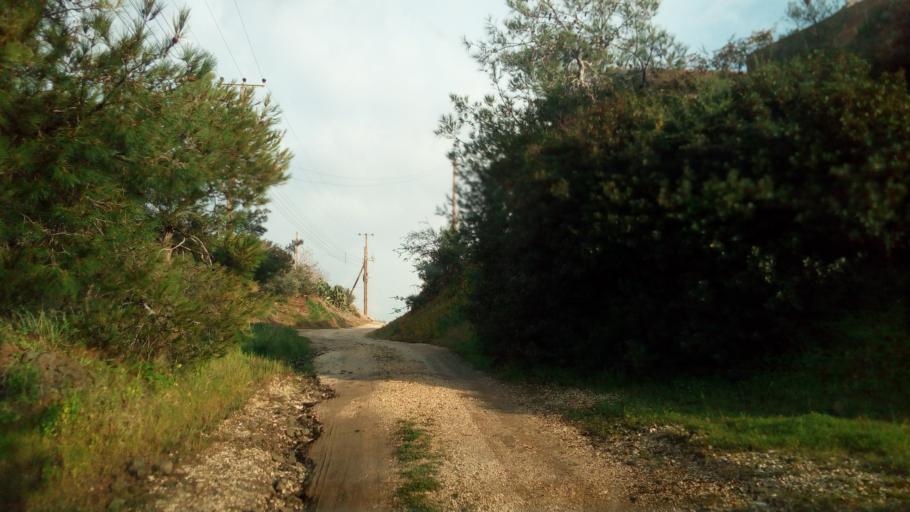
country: CY
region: Lefkosia
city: Kato Pyrgos
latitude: 35.1790
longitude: 32.6631
